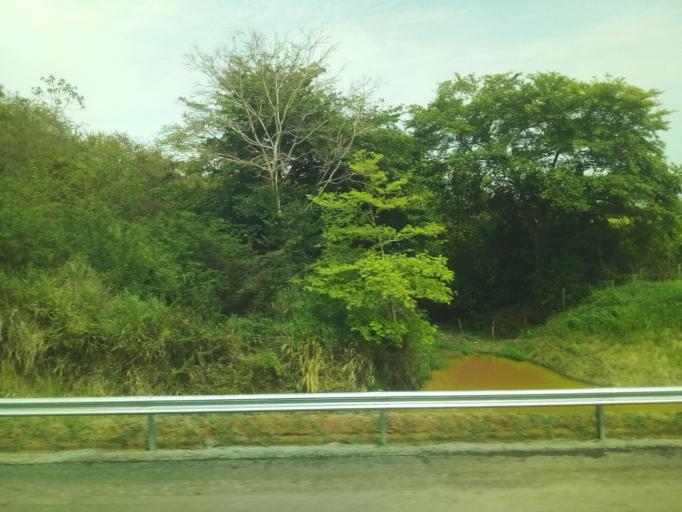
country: BR
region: Maranhao
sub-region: Anajatuba
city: Anajatuba
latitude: -3.4516
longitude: -44.5834
